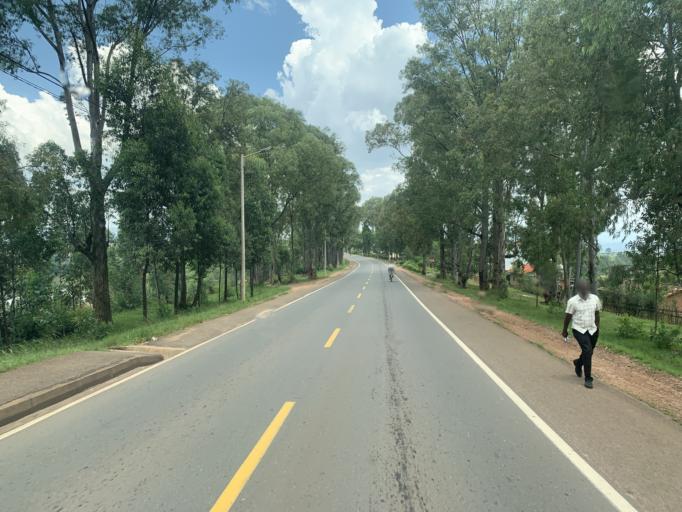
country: RW
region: Kigali
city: Kigali
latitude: -1.9987
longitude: 29.9073
